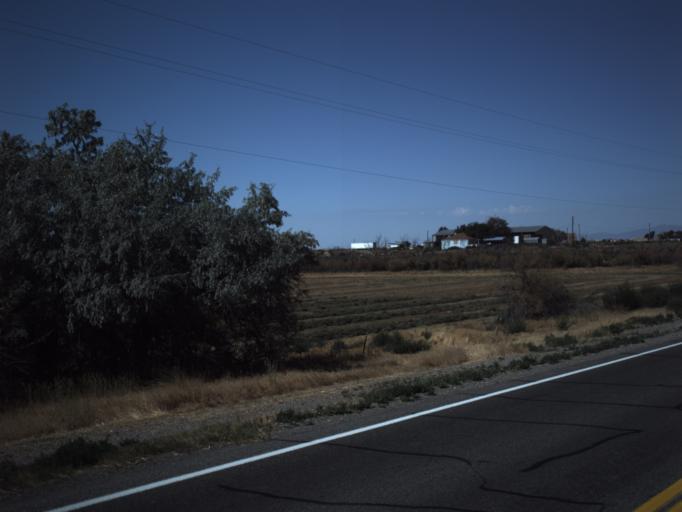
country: US
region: Utah
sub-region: Millard County
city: Delta
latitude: 39.3305
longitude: -112.6196
